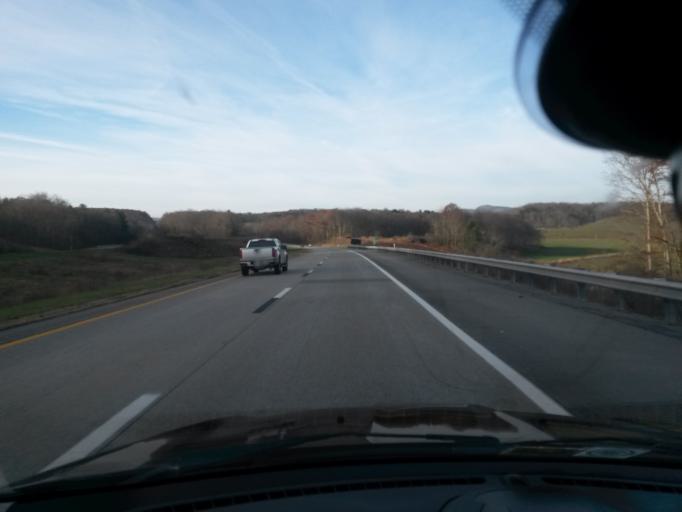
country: US
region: West Virginia
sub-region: Greenbrier County
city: Rainelle
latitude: 37.8872
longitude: -80.6714
